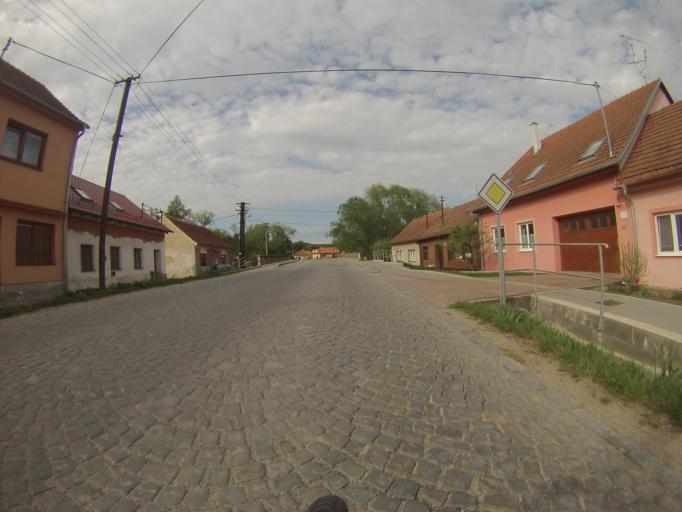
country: CZ
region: South Moravian
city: Veverska Bityska
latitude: 49.2775
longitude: 16.4379
